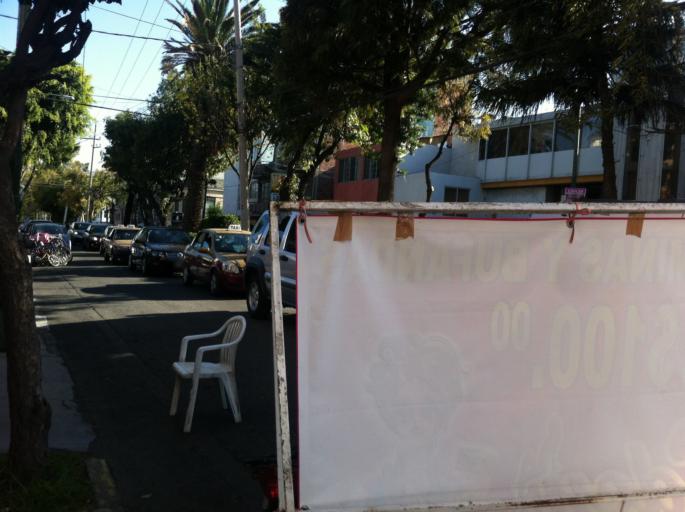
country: MX
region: Mexico
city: Colonia Lindavista
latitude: 19.4976
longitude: -99.1276
